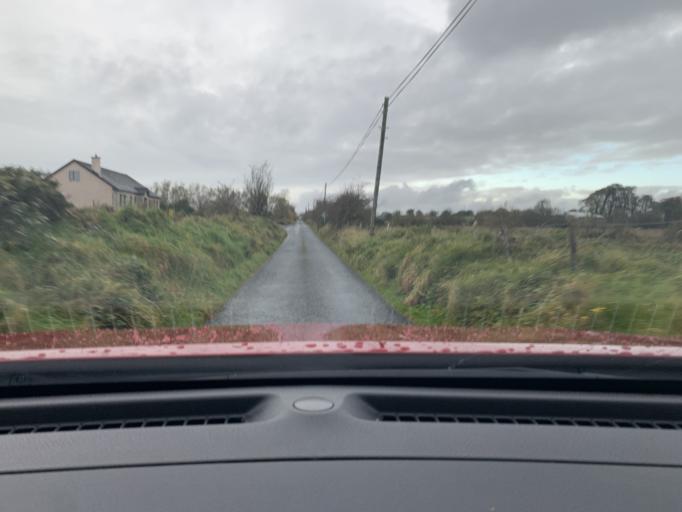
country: IE
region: Connaught
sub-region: Roscommon
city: Ballaghaderreen
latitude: 53.9653
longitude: -8.5488
